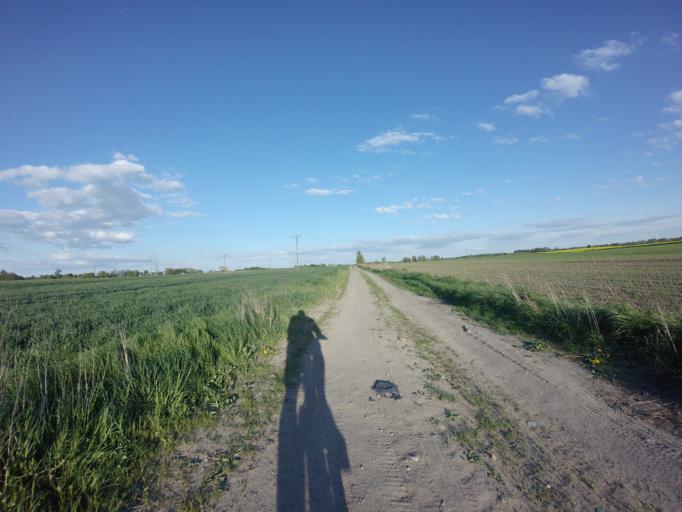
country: PL
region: West Pomeranian Voivodeship
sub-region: Powiat choszczenski
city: Choszczno
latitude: 53.1446
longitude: 15.4210
